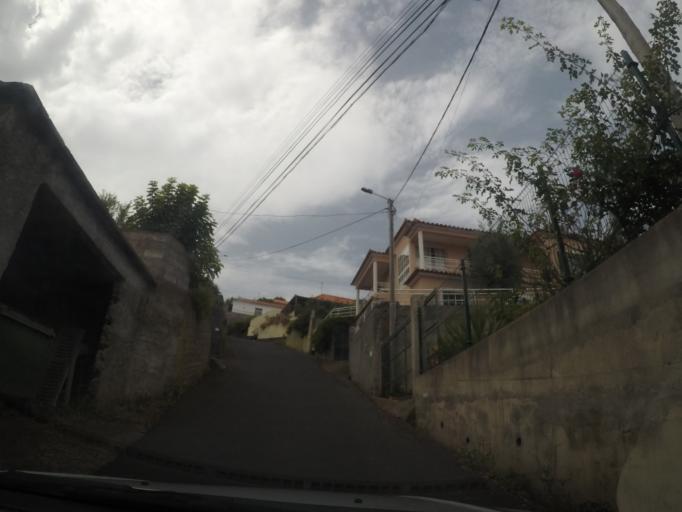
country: PT
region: Madeira
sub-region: Santa Cruz
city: Santa Cruz
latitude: 32.6876
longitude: -16.8087
